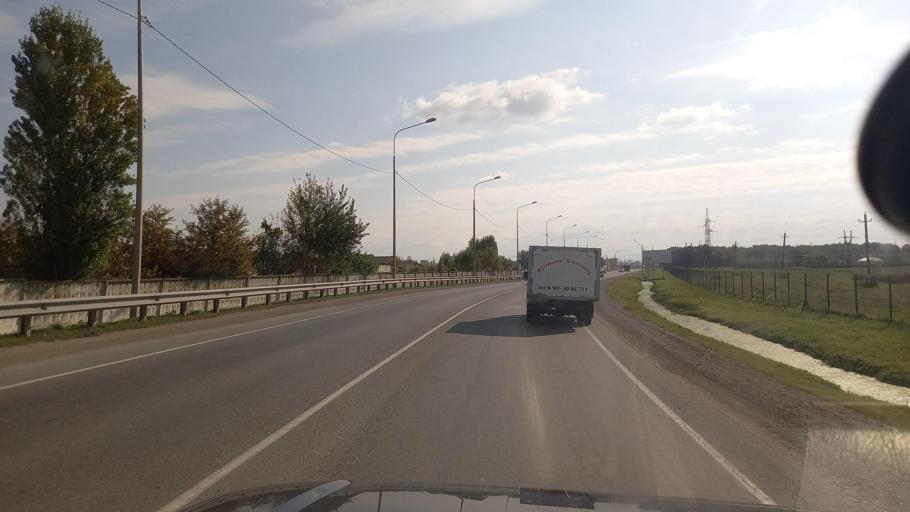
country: RU
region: Krasnodarskiy
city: Krymsk
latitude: 44.9118
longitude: 38.0165
